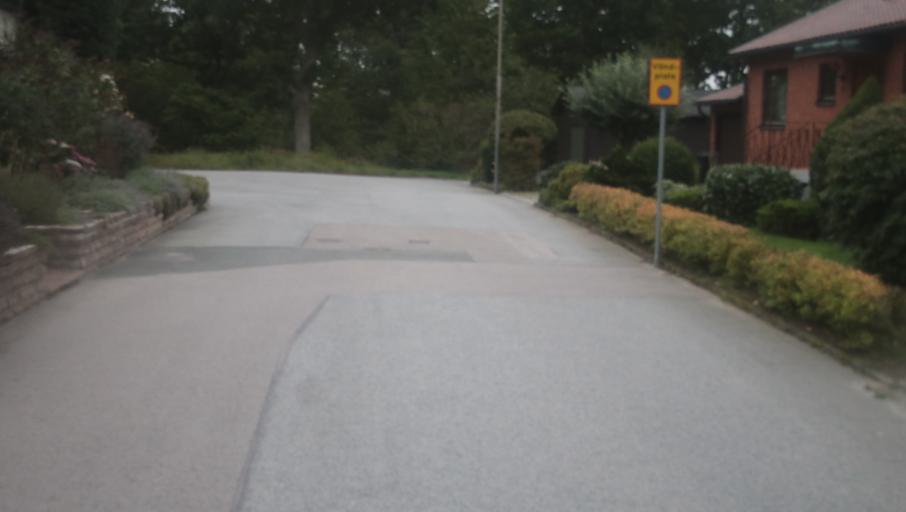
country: SE
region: Blekinge
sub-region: Karlshamns Kommun
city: Karlshamn
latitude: 56.1684
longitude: 14.8841
